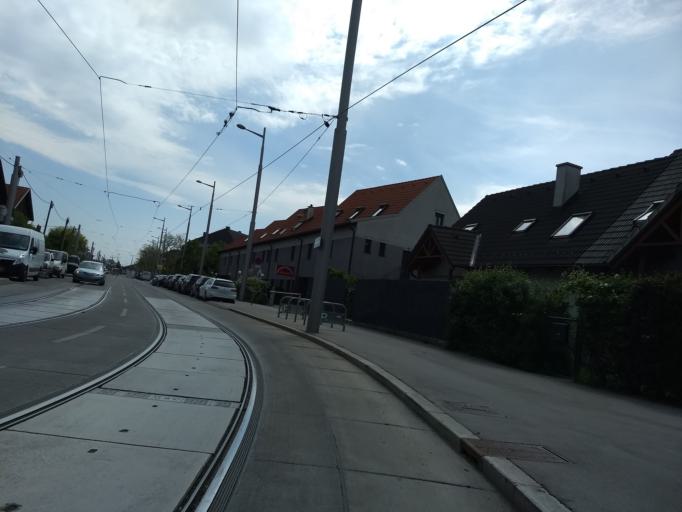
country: AT
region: Lower Austria
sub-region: Politischer Bezirk Wien-Umgebung
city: Gerasdorf bei Wien
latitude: 48.2383
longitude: 16.4847
